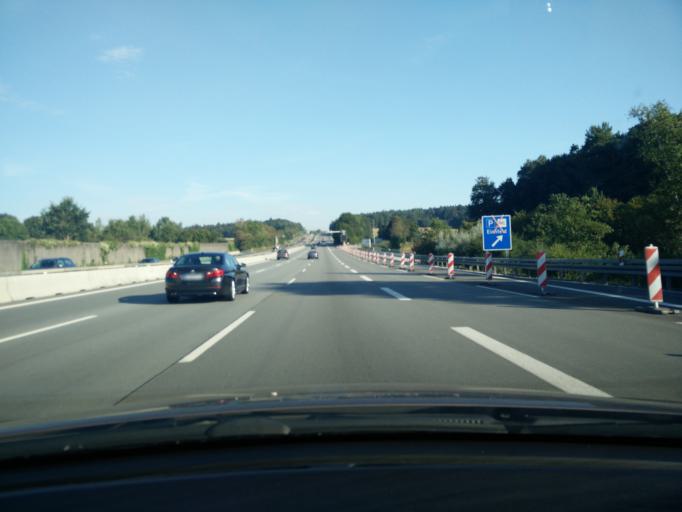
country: DE
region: Bavaria
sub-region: Upper Bavaria
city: Allershausen
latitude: 48.4614
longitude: 11.5900
